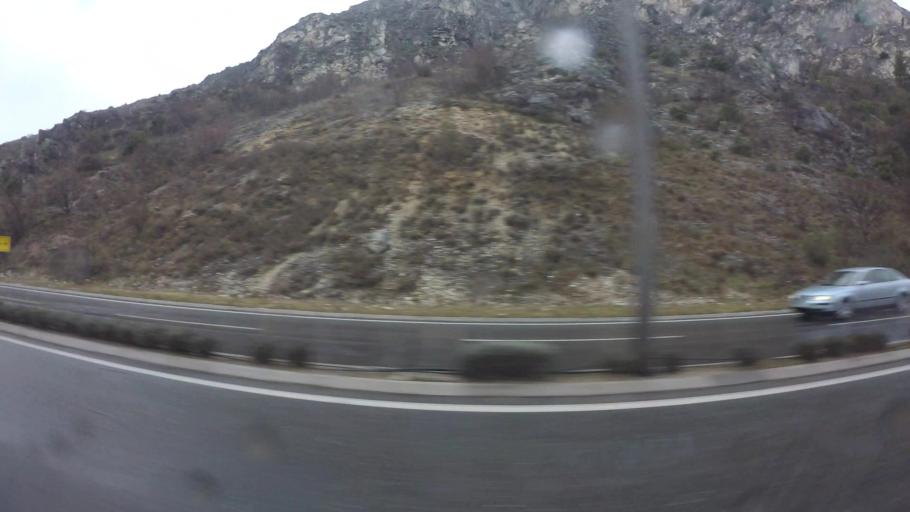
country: BA
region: Federation of Bosnia and Herzegovina
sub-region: Hercegovacko-Bosanski Kanton
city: Mostar
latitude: 43.3285
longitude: 17.8158
